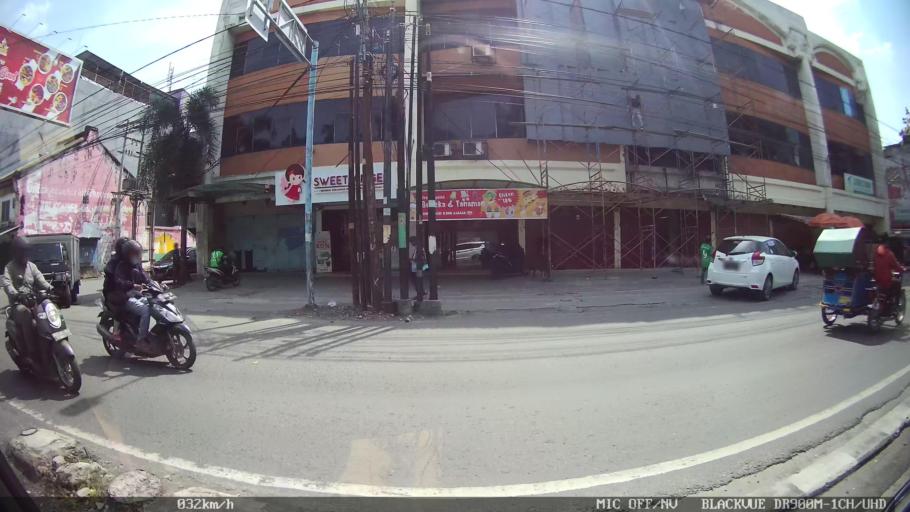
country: ID
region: North Sumatra
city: Medan
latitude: 3.5875
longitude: 98.6825
